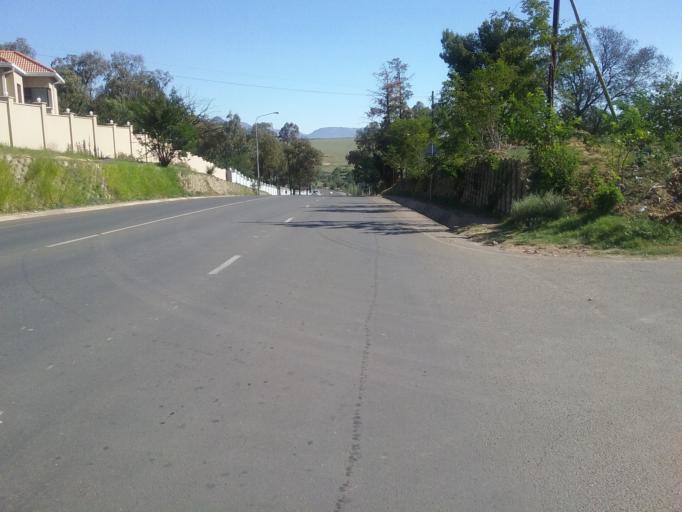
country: LS
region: Maseru
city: Maseru
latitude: -29.3049
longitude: 27.4661
